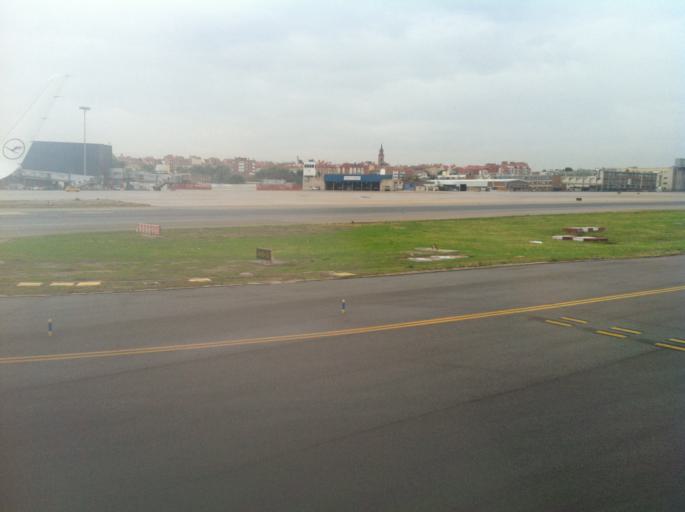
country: ES
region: Madrid
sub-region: Provincia de Madrid
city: Barajas de Madrid
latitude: 40.4741
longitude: -3.5678
